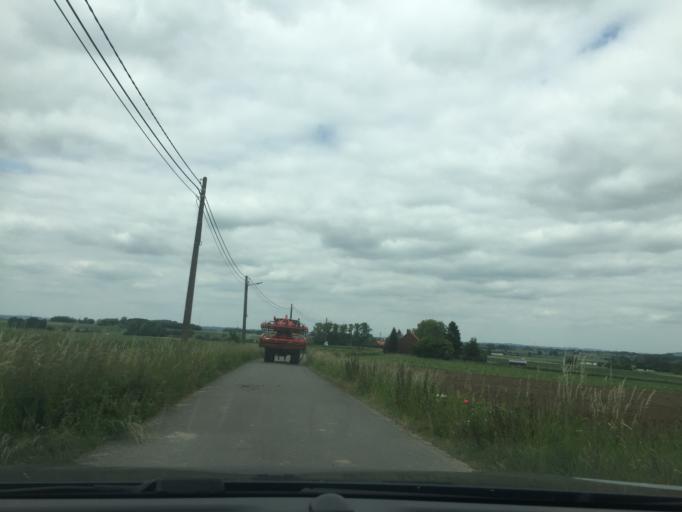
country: BE
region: Wallonia
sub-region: Province du Hainaut
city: Tournai
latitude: 50.6638
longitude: 3.4000
